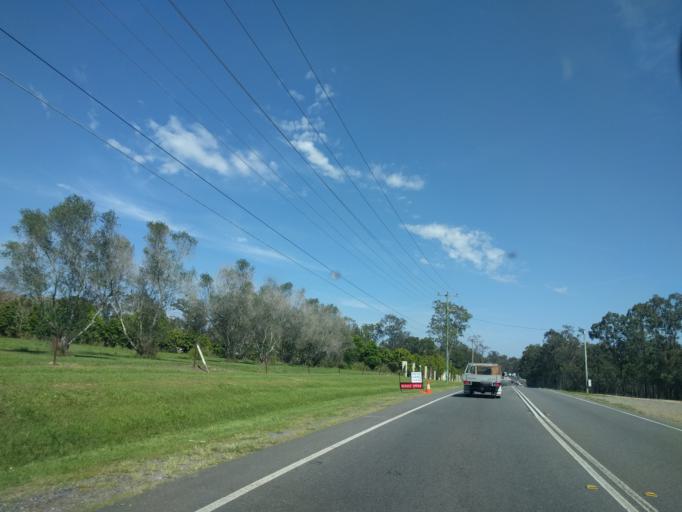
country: AU
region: Queensland
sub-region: Brisbane
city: Forest Lake
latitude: -27.6514
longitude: 152.9892
